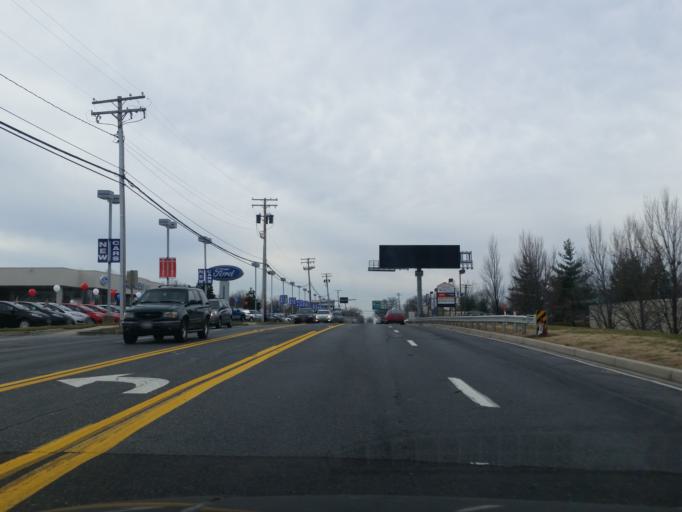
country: US
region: Maryland
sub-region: Prince George's County
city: South Laurel
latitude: 39.0752
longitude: -76.8695
